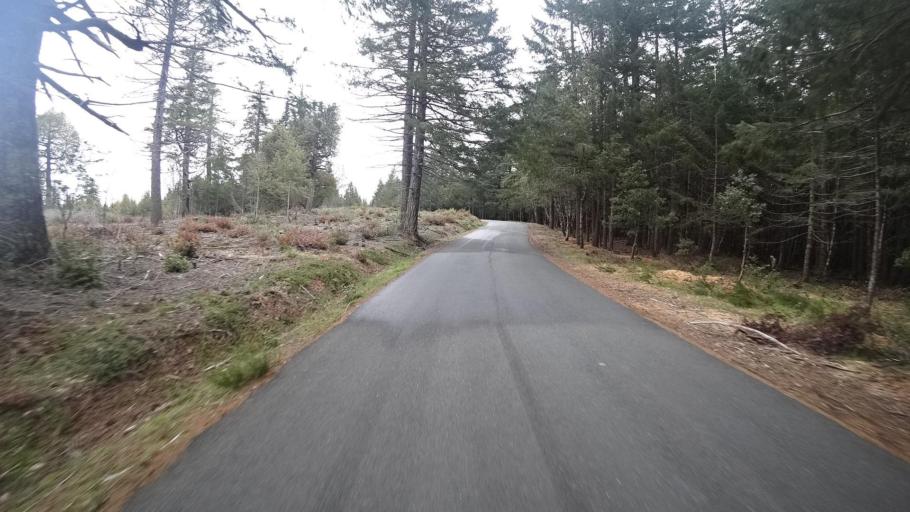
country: US
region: California
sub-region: Humboldt County
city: Willow Creek
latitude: 41.2012
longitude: -123.8030
